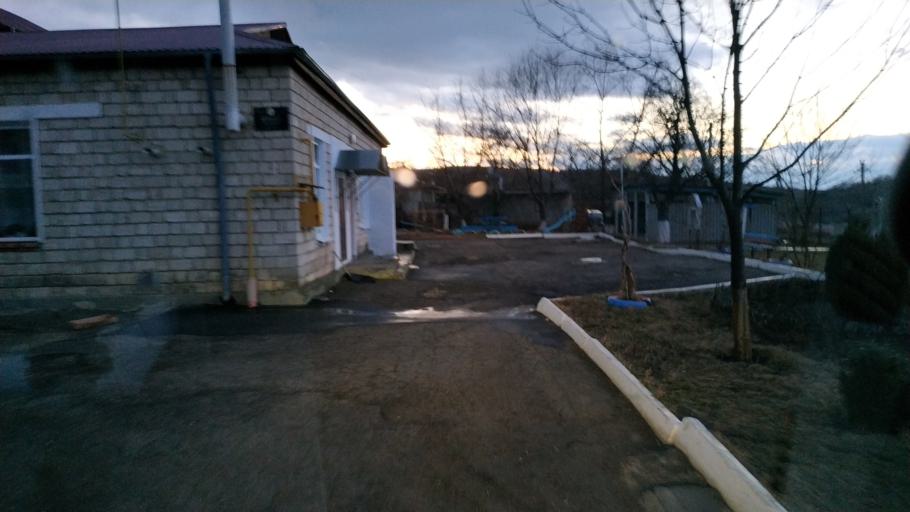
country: MD
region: Taraclia
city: Telenesti
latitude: 47.3721
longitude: 28.3775
